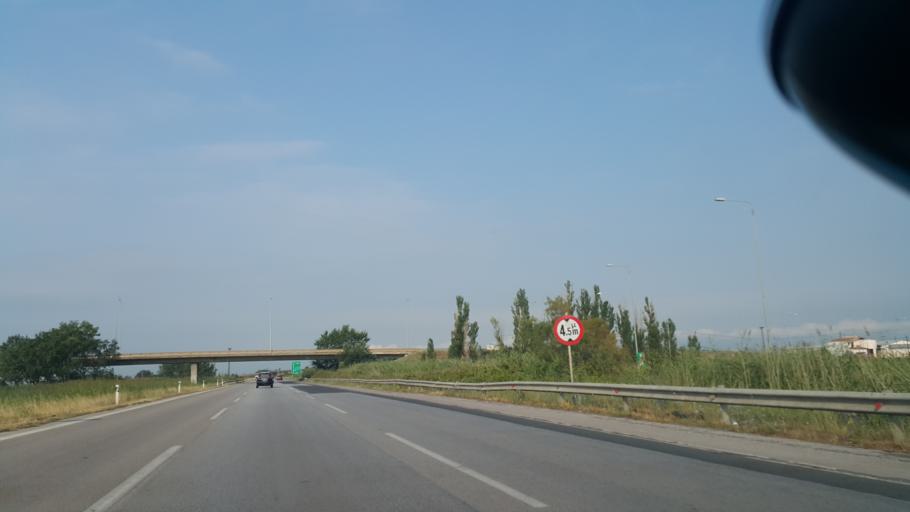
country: GR
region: Central Macedonia
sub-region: Nomos Thessalonikis
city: Chalastra
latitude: 40.6150
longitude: 22.7445
